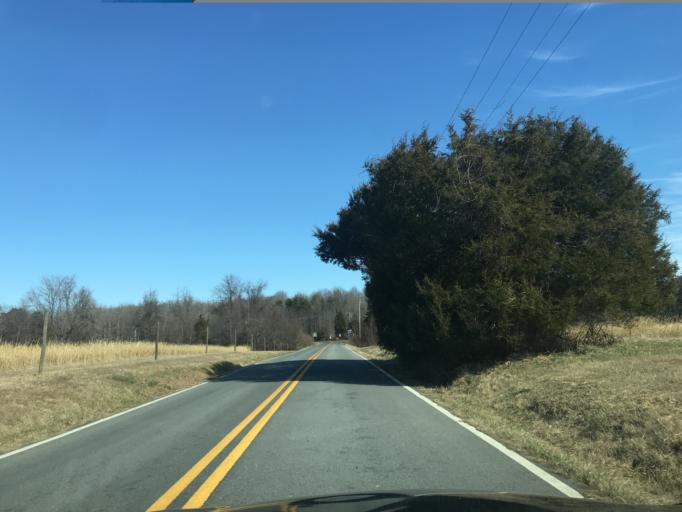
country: US
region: Virginia
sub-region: Prince William County
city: Cherry Hill
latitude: 38.5190
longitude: -77.2356
